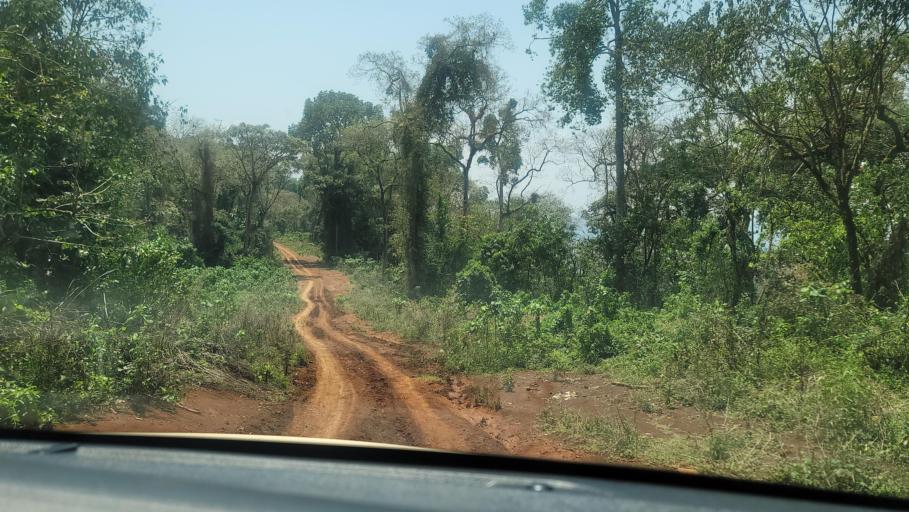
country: ET
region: Southern Nations, Nationalities, and People's Region
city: Bonga
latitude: 7.5459
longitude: 36.1771
